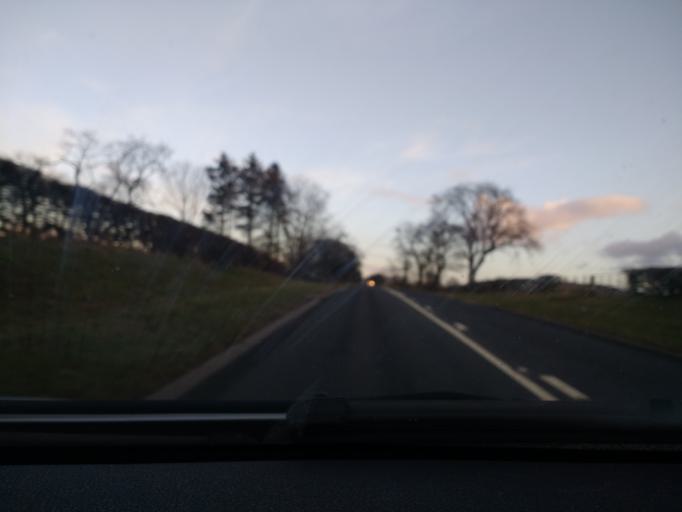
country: GB
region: England
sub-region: Cumbria
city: Penrith
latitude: 54.7264
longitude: -2.8985
